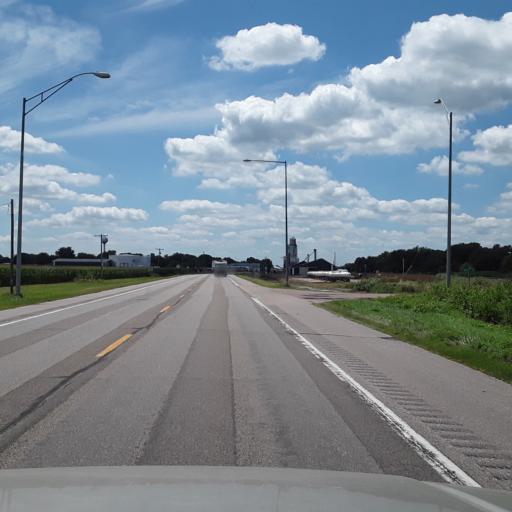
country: US
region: Nebraska
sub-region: Nance County
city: Genoa
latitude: 41.3193
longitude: -97.6553
